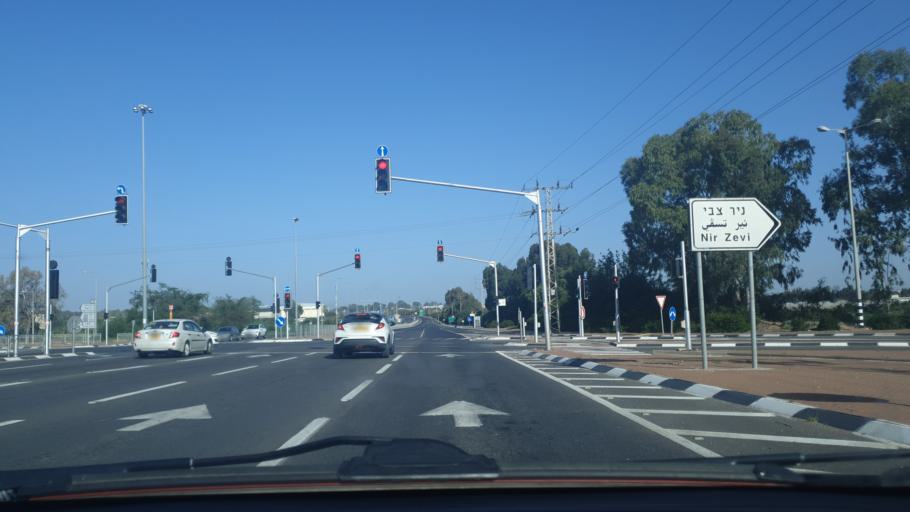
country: IL
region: Central District
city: Ramla
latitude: 31.9512
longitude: 34.8569
